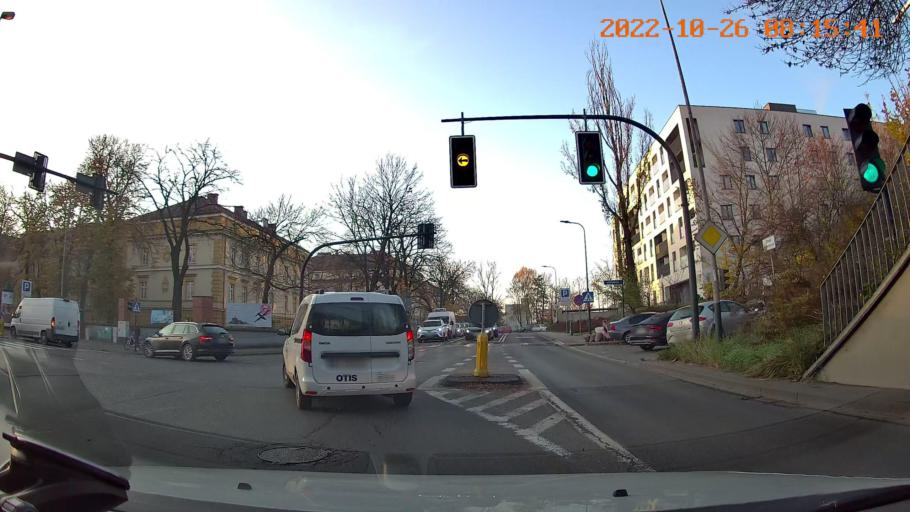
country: PL
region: Lesser Poland Voivodeship
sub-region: Krakow
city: Krakow
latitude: 50.0819
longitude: 19.9153
